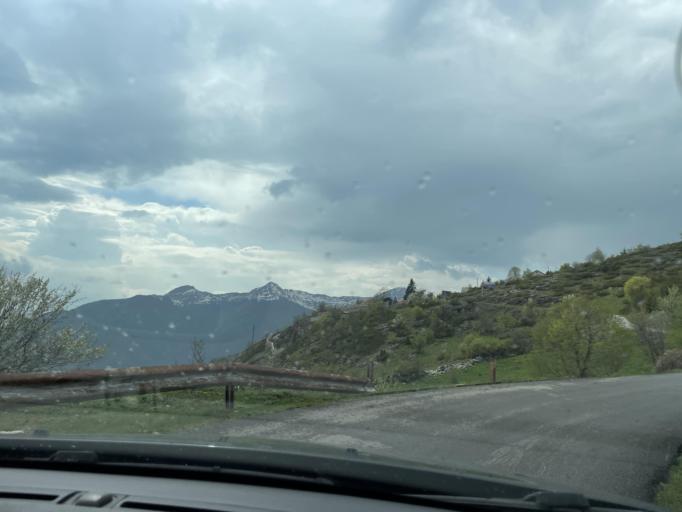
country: MK
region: Opstina Rostusa
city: Rostusha
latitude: 41.5935
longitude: 20.6619
